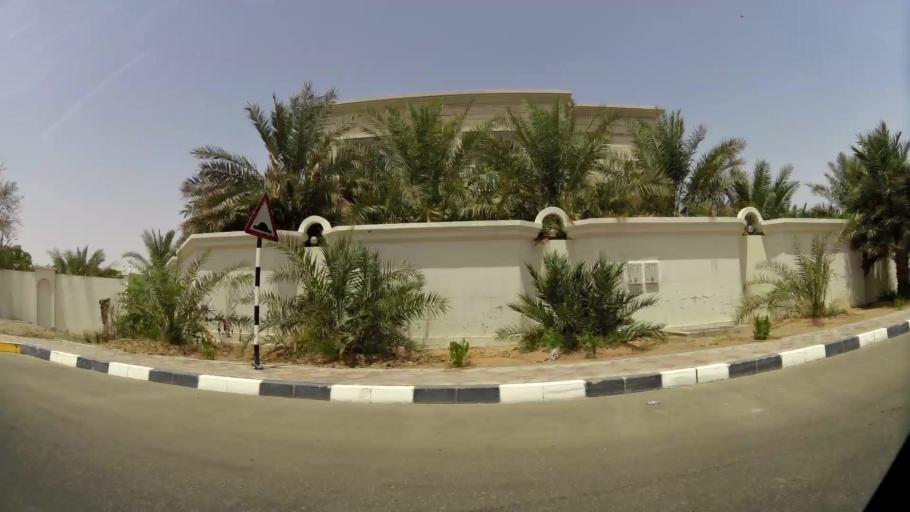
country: AE
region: Abu Dhabi
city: Al Ain
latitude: 24.1953
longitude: 55.7340
